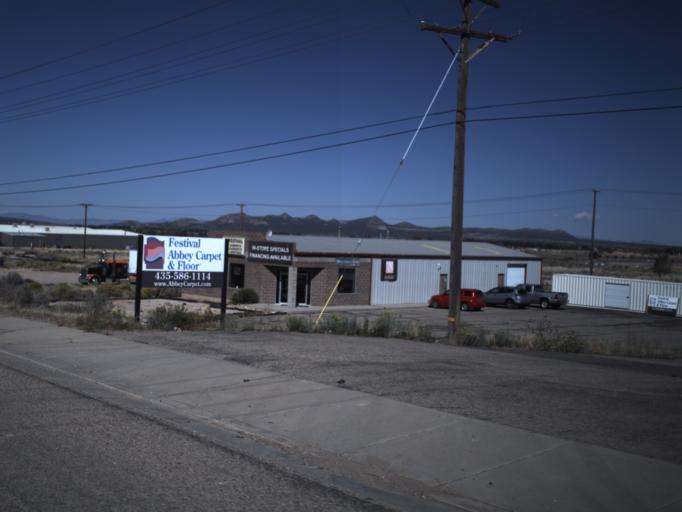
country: US
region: Utah
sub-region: Iron County
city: Cedar City
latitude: 37.6850
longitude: -113.0984
